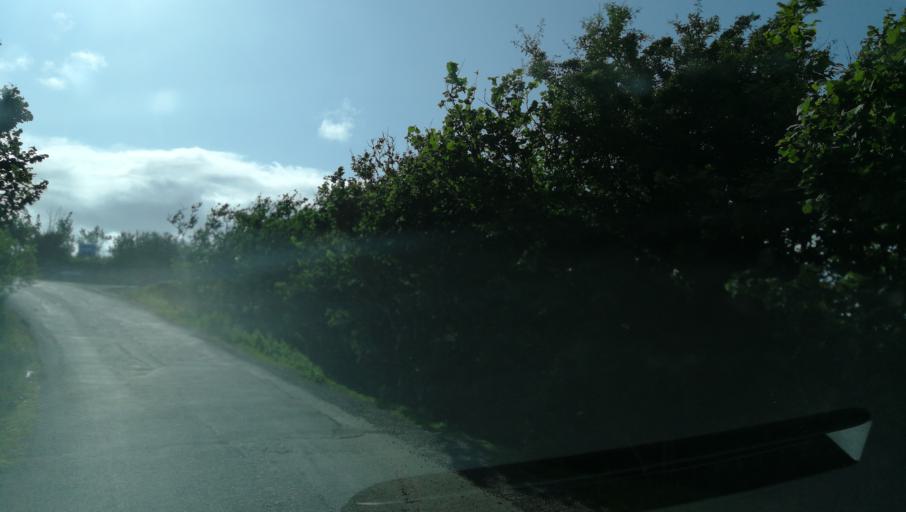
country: GB
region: Scotland
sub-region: Highland
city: Isle of Skye
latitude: 57.4317
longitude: -6.5774
